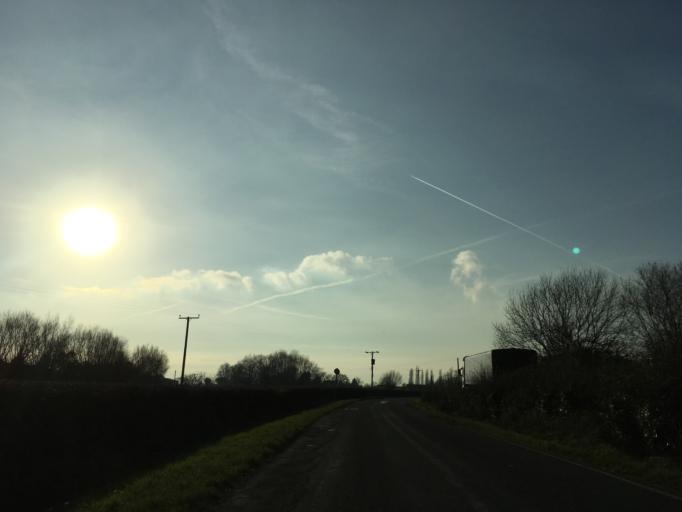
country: GB
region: Wales
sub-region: Newport
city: Goldcliff
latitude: 51.5600
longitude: -2.9285
